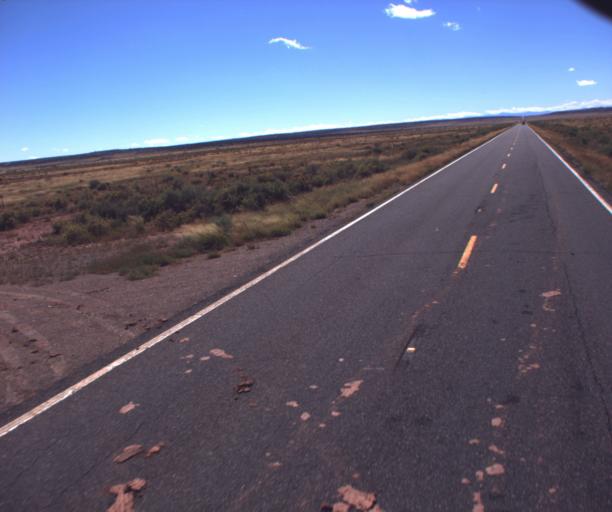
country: US
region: Arizona
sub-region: Apache County
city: Saint Johns
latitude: 34.7151
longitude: -109.2629
